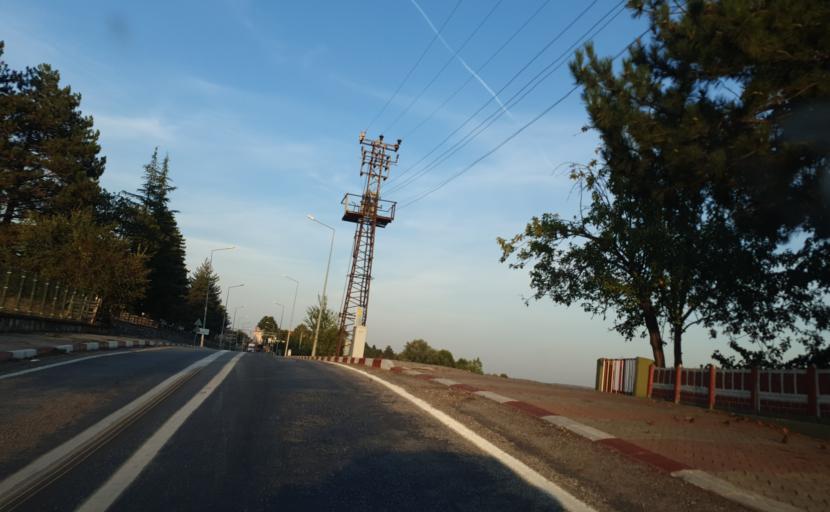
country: TR
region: Kirklareli
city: Sergen
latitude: 41.8214
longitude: 27.7579
